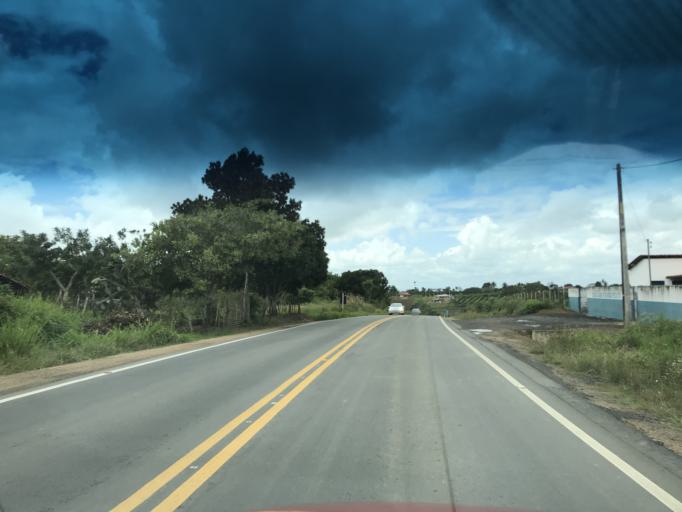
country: BR
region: Bahia
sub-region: Conceicao Do Almeida
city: Conceicao do Almeida
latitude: -12.6968
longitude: -39.2422
